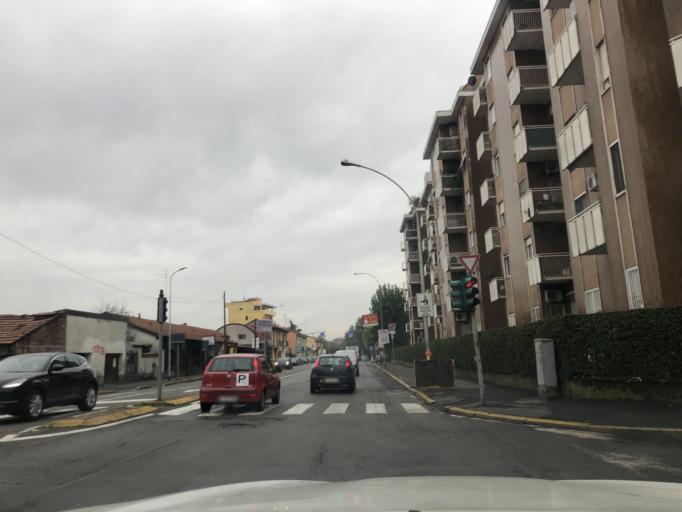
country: IT
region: Lombardy
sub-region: Citta metropolitana di Milano
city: Cesano Boscone
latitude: 45.4462
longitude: 9.0990
